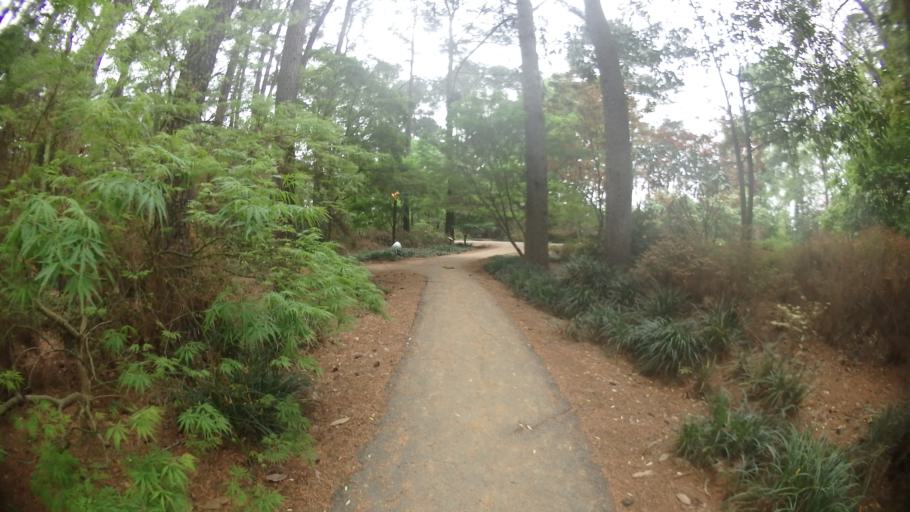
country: US
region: Texas
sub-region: Nacogdoches County
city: Nacogdoches
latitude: 31.6205
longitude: -94.6402
